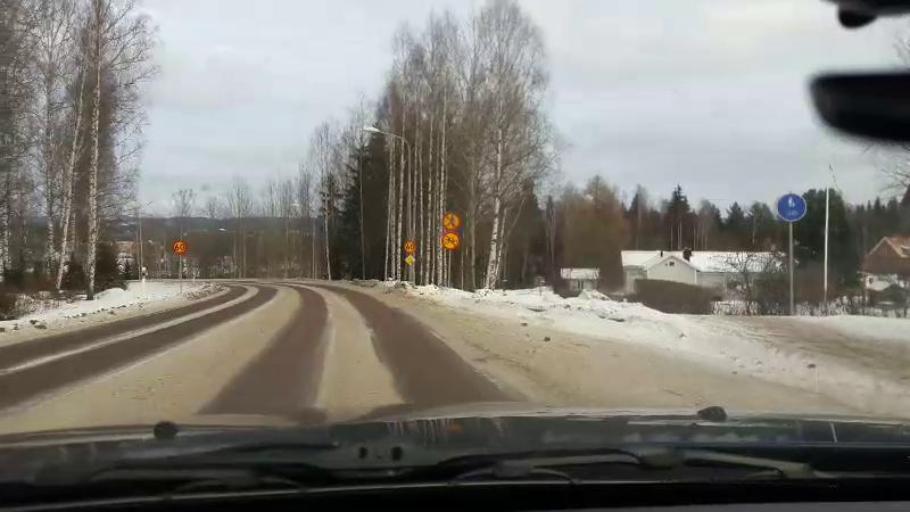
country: SE
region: Gaevleborg
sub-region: Bollnas Kommun
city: Bollnas
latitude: 61.3338
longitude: 16.3915
